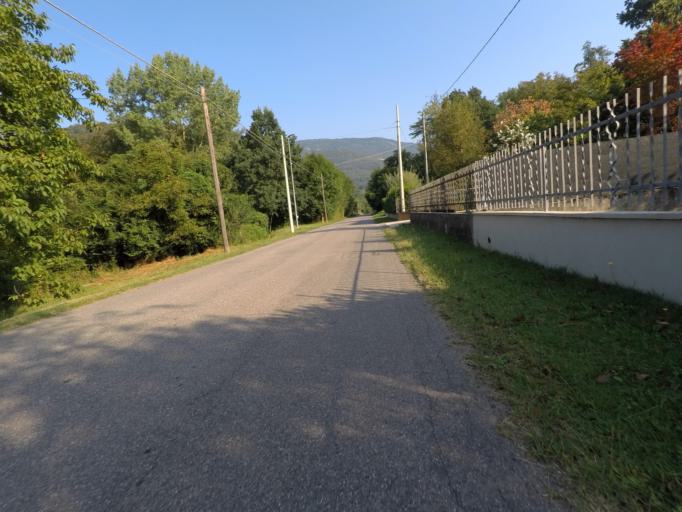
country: IT
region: Friuli Venezia Giulia
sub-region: Provincia di Udine
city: Forgaria nel Friuli
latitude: 46.2088
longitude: 12.9580
